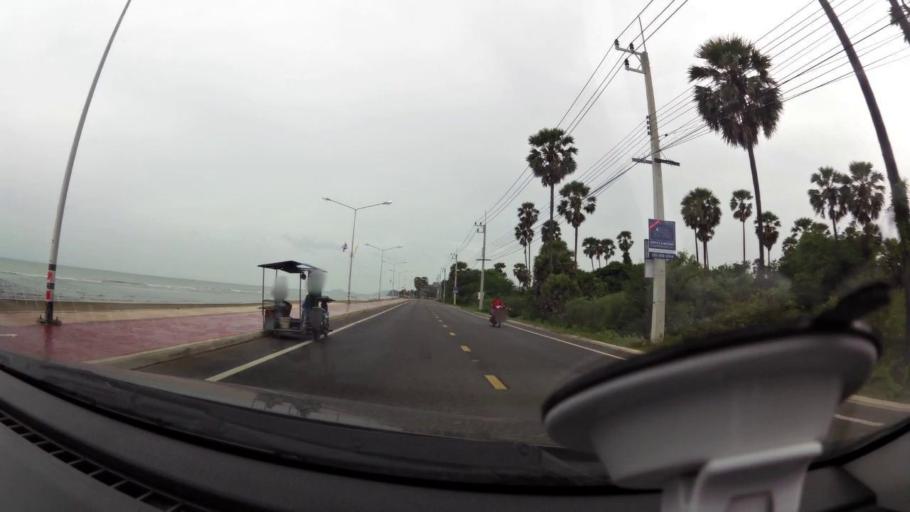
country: TH
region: Prachuap Khiri Khan
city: Pran Buri
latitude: 12.3748
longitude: 100.0002
